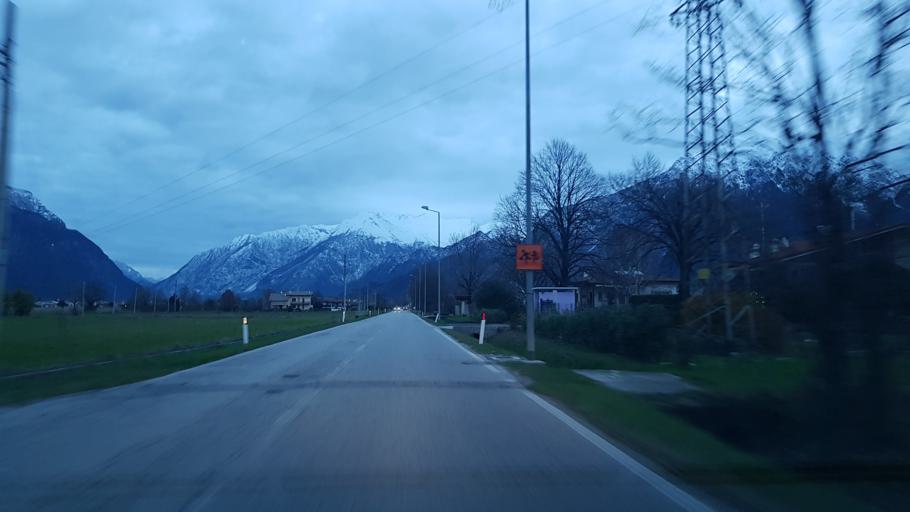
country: IT
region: Friuli Venezia Giulia
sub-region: Provincia di Udine
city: Osoppo
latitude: 46.2714
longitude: 13.0956
